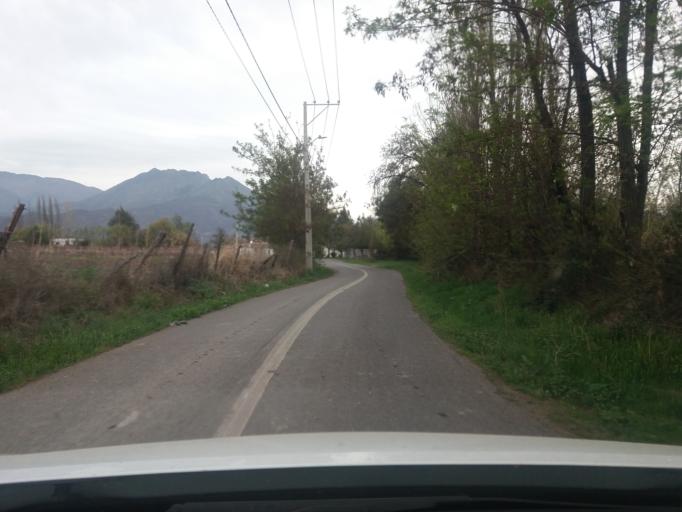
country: CL
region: Valparaiso
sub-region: Provincia de Los Andes
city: Los Andes
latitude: -32.8550
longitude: -70.6453
